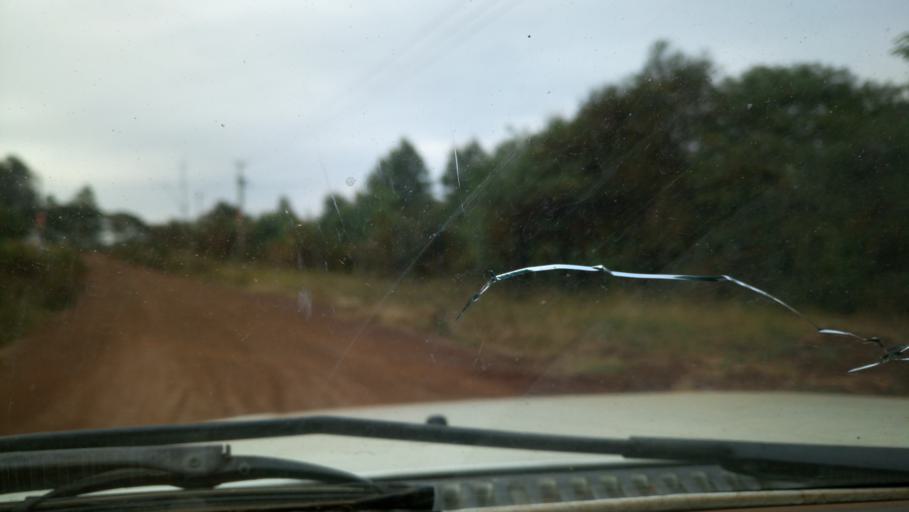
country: KE
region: Murang'a District
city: Maragua
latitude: -0.7674
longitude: 37.1547
